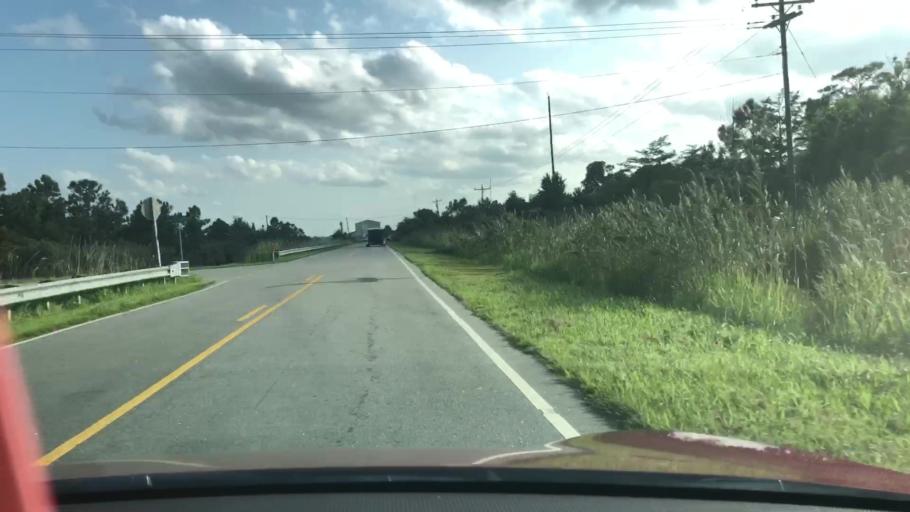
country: US
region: North Carolina
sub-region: Dare County
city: Wanchese
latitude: 35.7008
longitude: -75.7714
